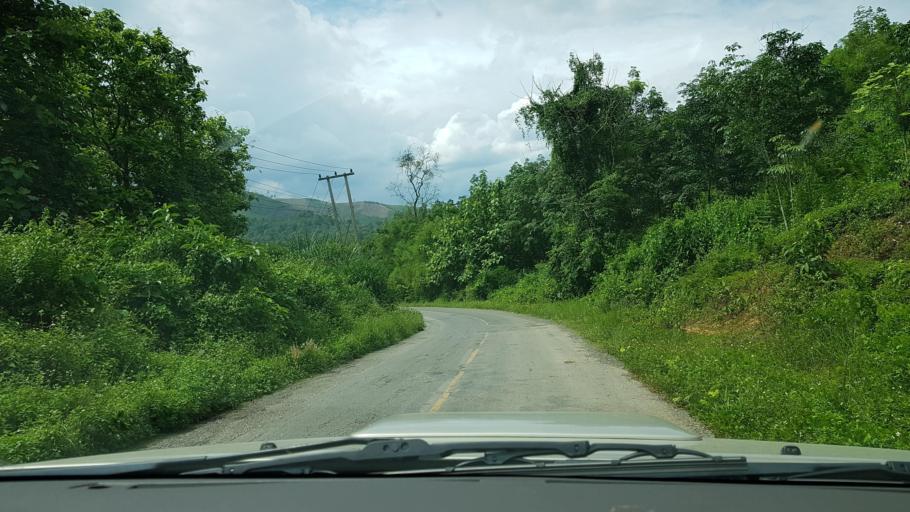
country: LA
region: Loungnamtha
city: Muang Nale
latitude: 20.2445
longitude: 101.5773
